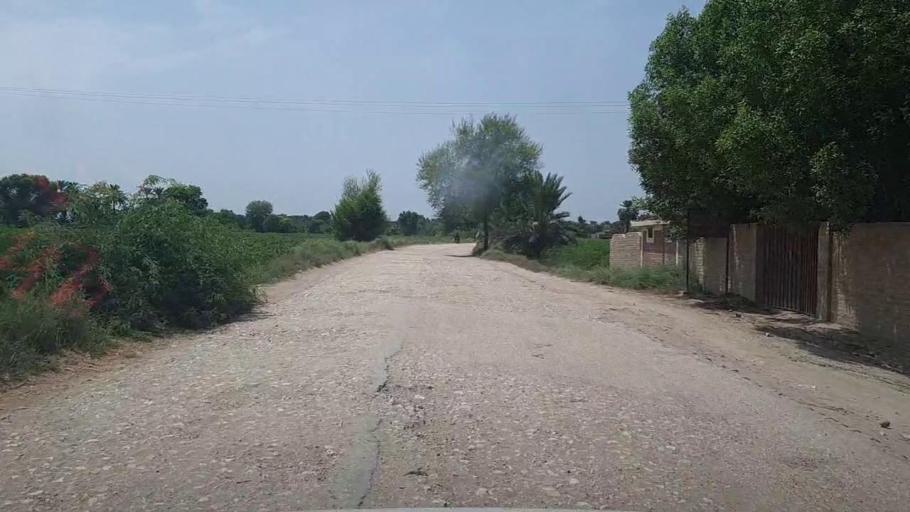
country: PK
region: Sindh
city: Pano Aqil
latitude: 27.8528
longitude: 69.1375
